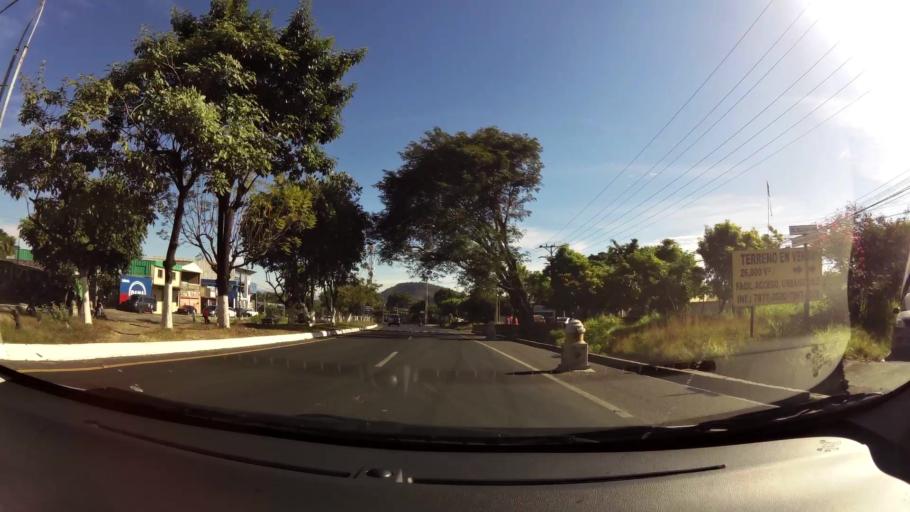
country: SV
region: Santa Ana
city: Santa Ana
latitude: 13.9788
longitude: -89.5559
